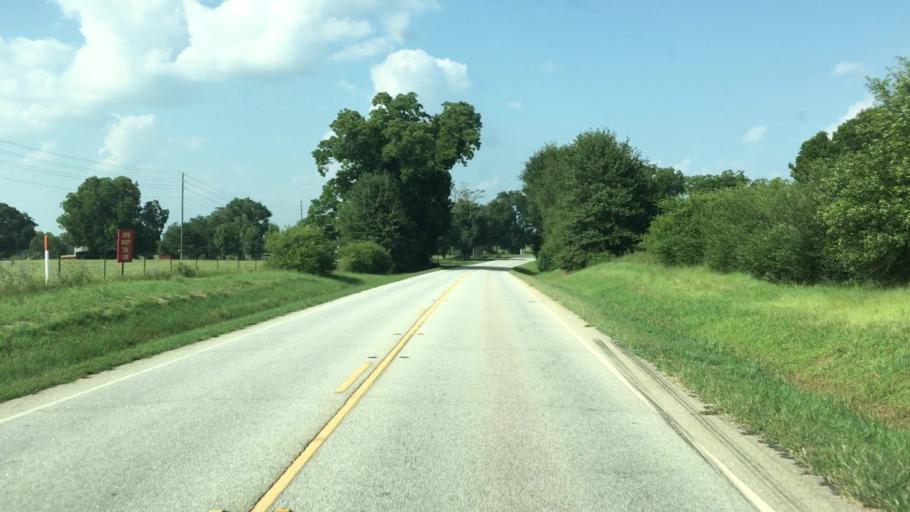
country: US
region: Georgia
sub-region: Newton County
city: Covington
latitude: 33.4853
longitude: -83.7431
